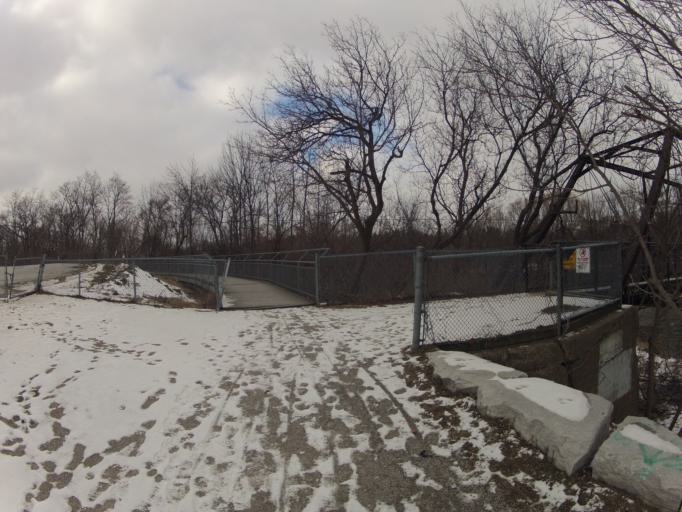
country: CA
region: Ontario
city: Mississauga
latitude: 43.5742
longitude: -79.6941
